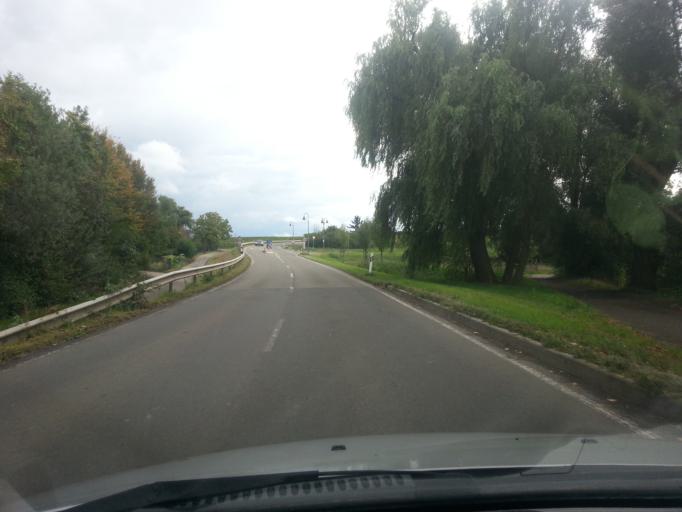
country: DE
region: Rheinland-Pfalz
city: Freinsheim
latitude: 49.5040
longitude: 8.2200
